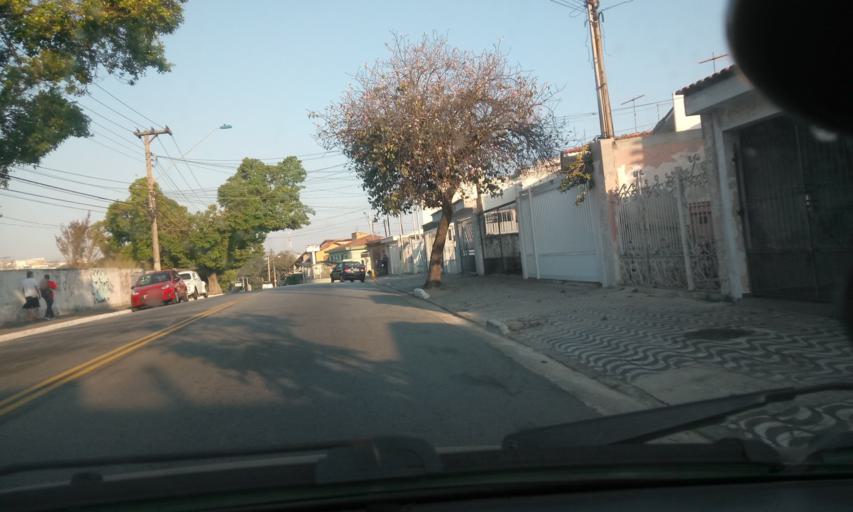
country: BR
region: Sao Paulo
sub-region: Sao Caetano Do Sul
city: Sao Caetano do Sul
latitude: -23.6367
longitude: -46.5765
